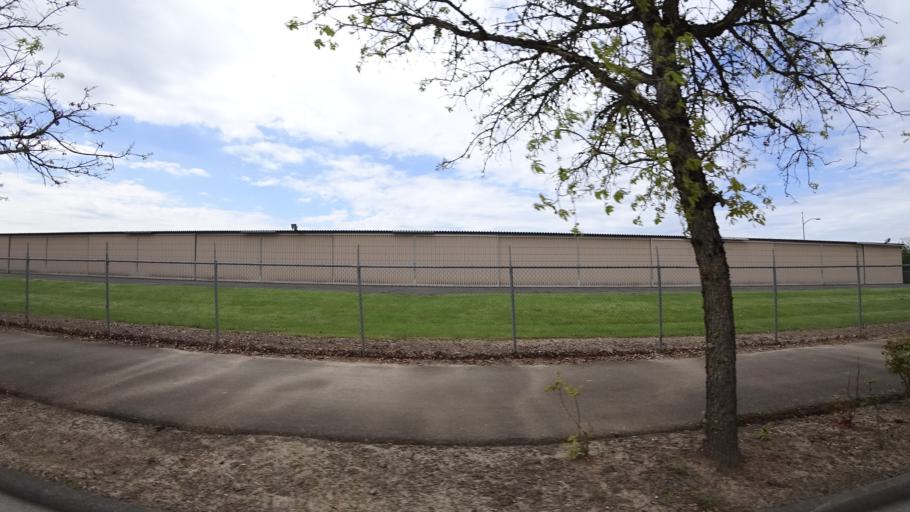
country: US
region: Oregon
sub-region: Washington County
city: Hillsboro
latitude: 45.5386
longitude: -122.9402
